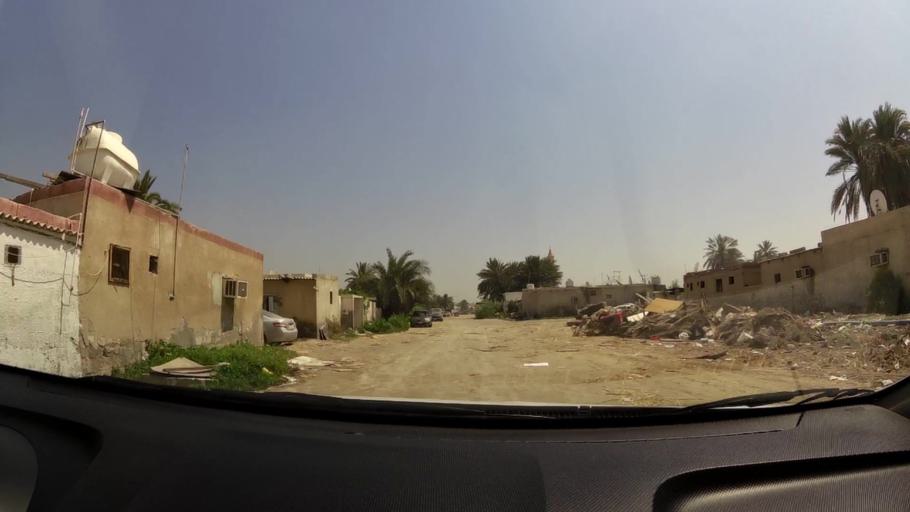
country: AE
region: Umm al Qaywayn
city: Umm al Qaywayn
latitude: 25.5602
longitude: 55.5520
